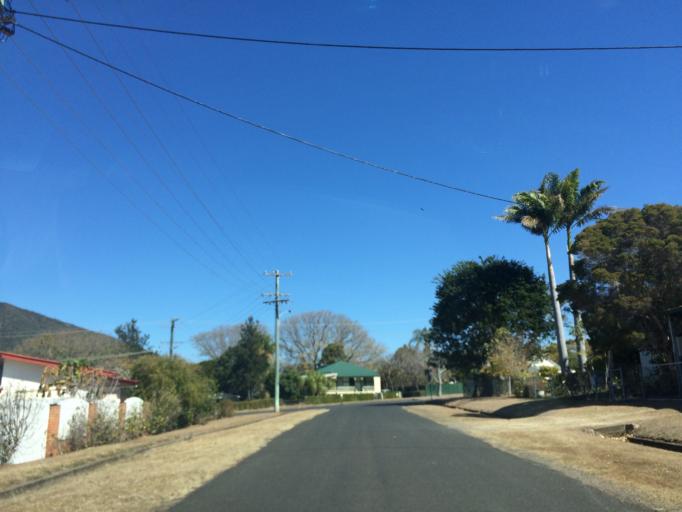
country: AU
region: Queensland
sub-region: Ipswich
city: Thagoona
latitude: -27.9805
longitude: 152.5477
